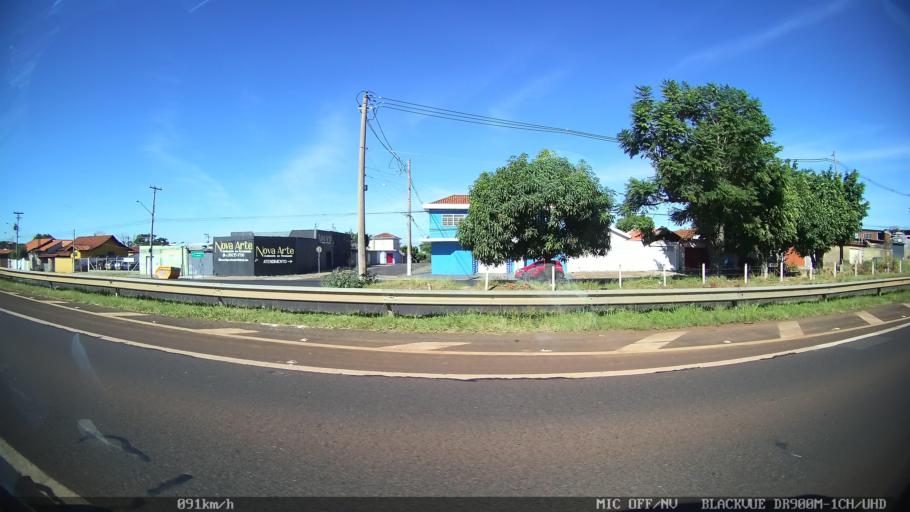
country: BR
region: Sao Paulo
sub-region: Franca
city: Franca
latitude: -20.5733
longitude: -47.3755
